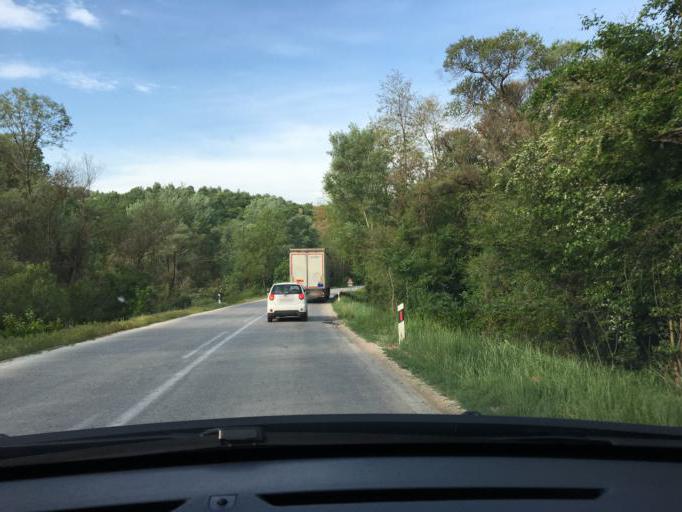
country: MK
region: Kriva Palanka
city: Kriva Palanka
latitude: 42.1747
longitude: 22.2360
